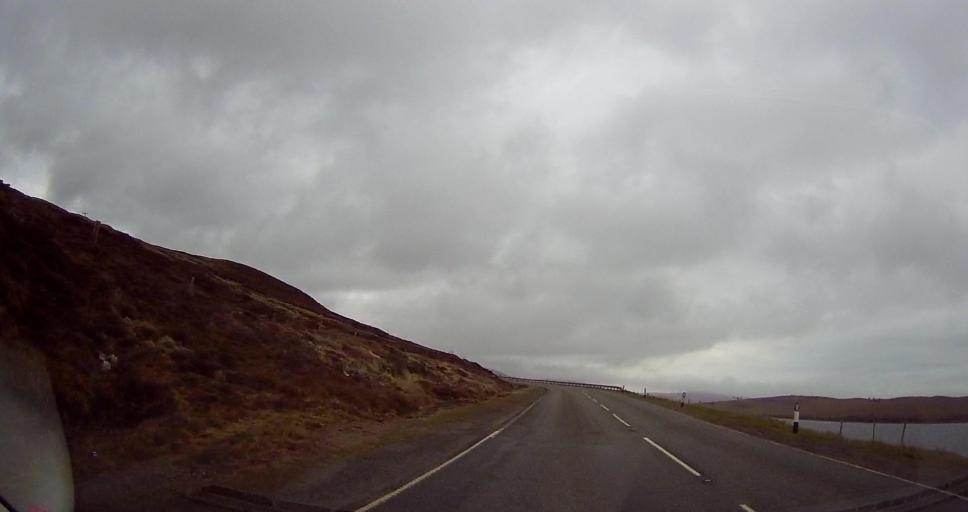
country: GB
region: Scotland
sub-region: Shetland Islands
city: Lerwick
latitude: 60.2490
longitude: -1.2263
